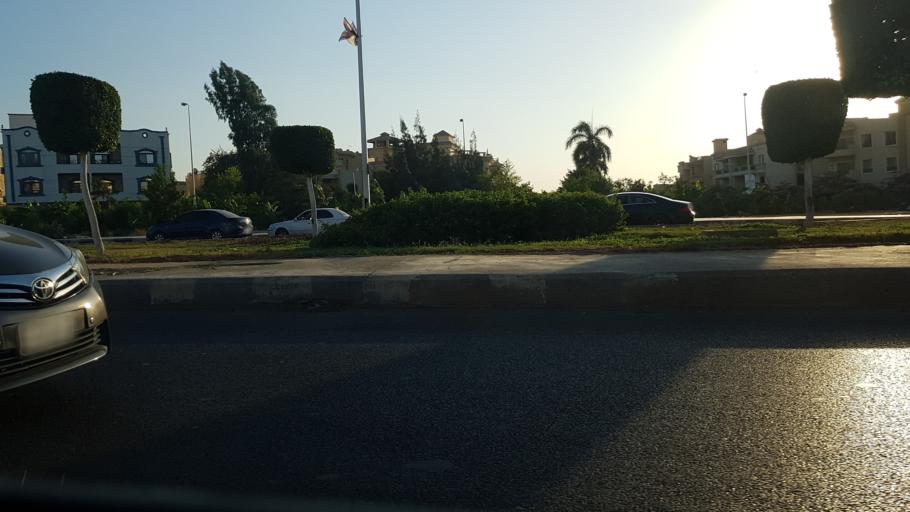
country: EG
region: Muhafazat al Qalyubiyah
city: Al Khankah
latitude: 30.0324
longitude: 31.4396
